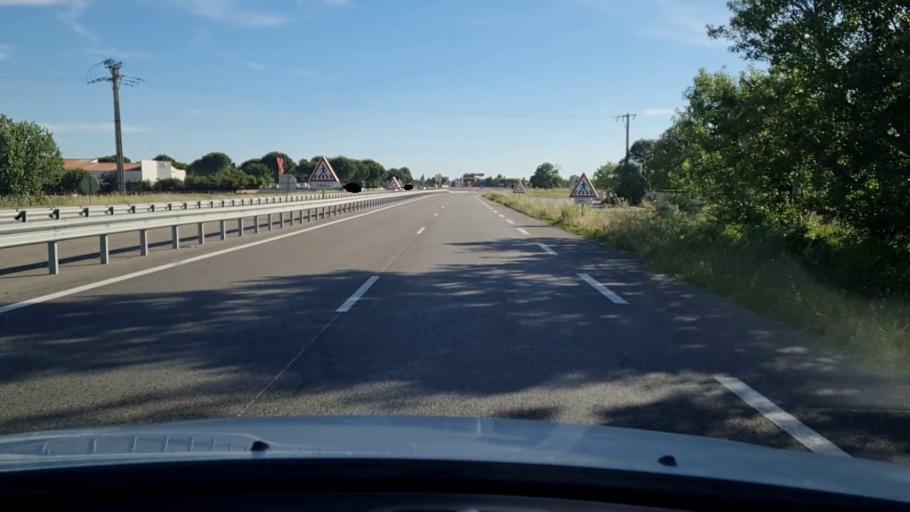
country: FR
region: Languedoc-Roussillon
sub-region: Departement du Gard
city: Aimargues
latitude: 43.6805
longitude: 4.2144
